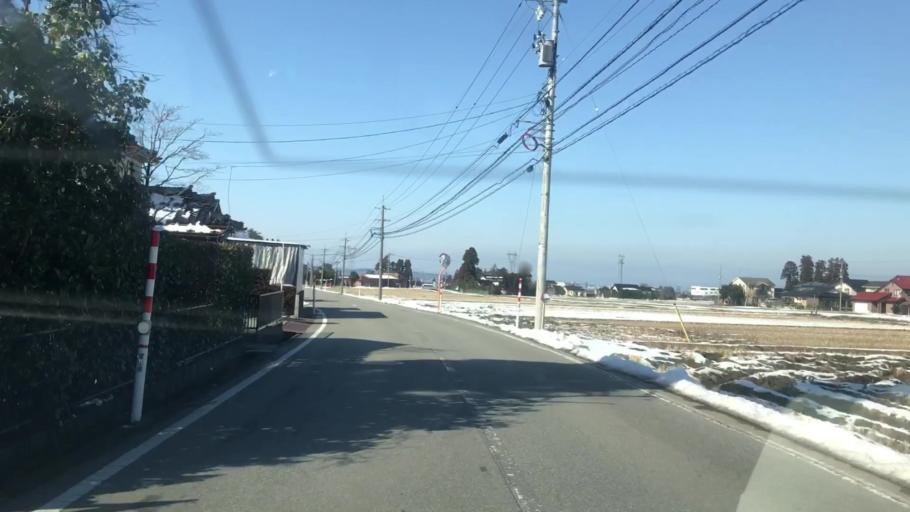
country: JP
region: Toyama
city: Toyama-shi
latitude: 36.6277
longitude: 137.2746
